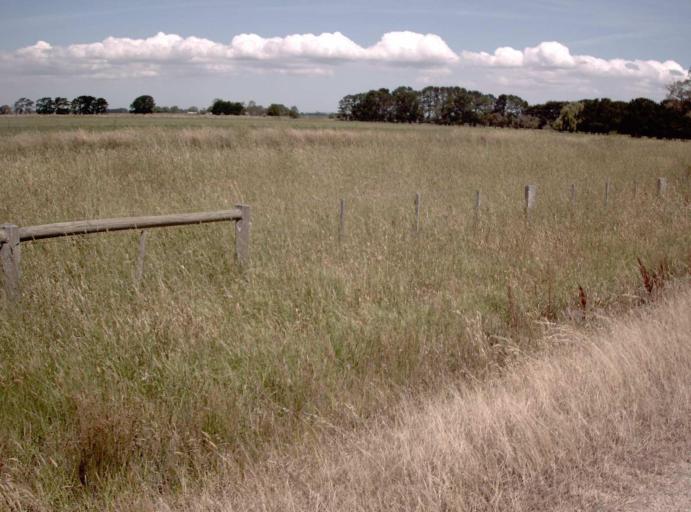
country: AU
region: Victoria
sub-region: Wellington
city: Heyfield
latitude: -38.0322
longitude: 146.8789
